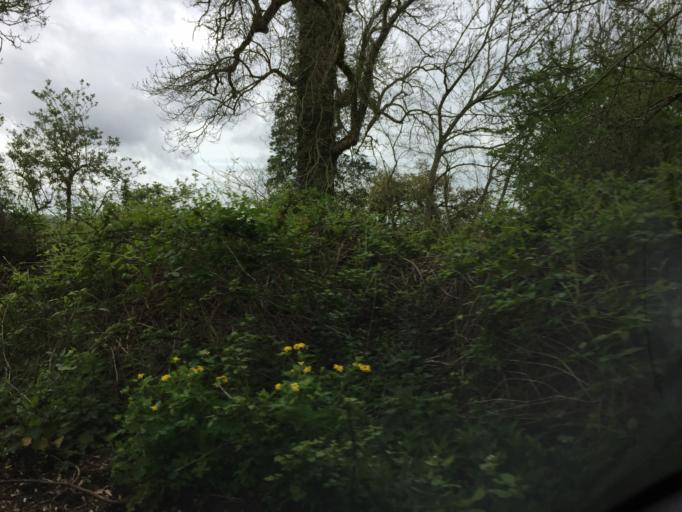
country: GB
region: England
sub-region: Bath and North East Somerset
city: Bath
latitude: 51.3562
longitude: -2.3393
